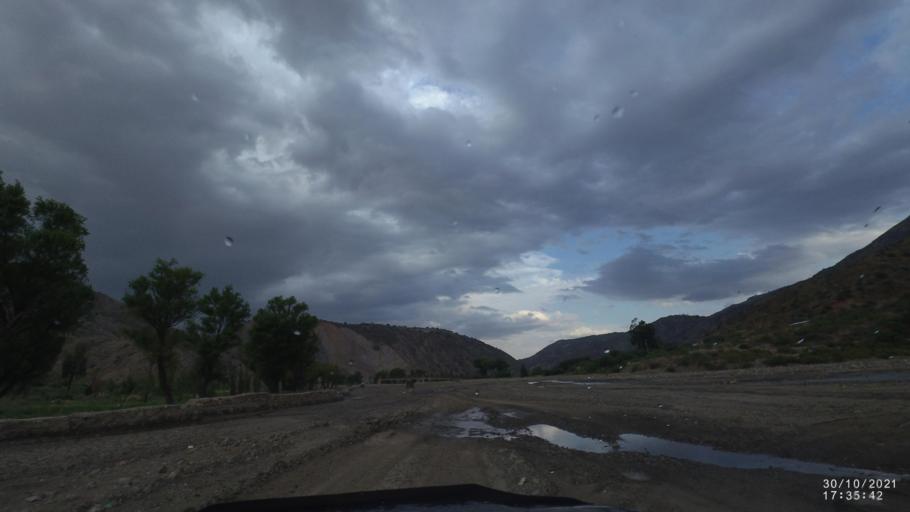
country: BO
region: Cochabamba
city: Sipe Sipe
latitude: -17.5257
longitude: -66.5701
